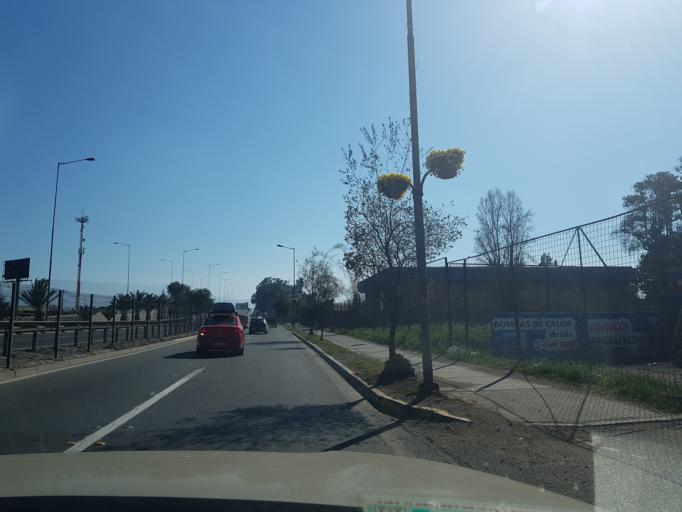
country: CL
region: Santiago Metropolitan
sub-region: Provincia de Santiago
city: Lo Prado
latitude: -33.3717
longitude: -70.7347
